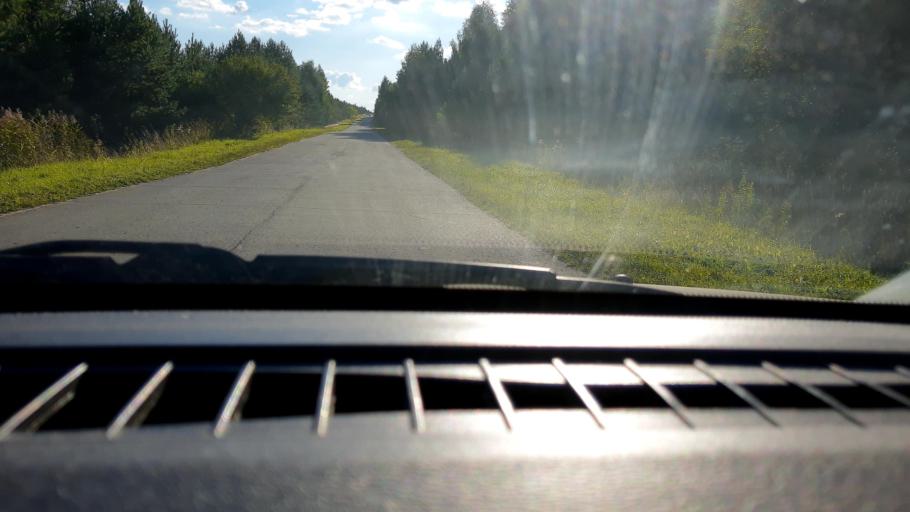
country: RU
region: Nizjnij Novgorod
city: Surovatikha
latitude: 55.9428
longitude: 43.9096
